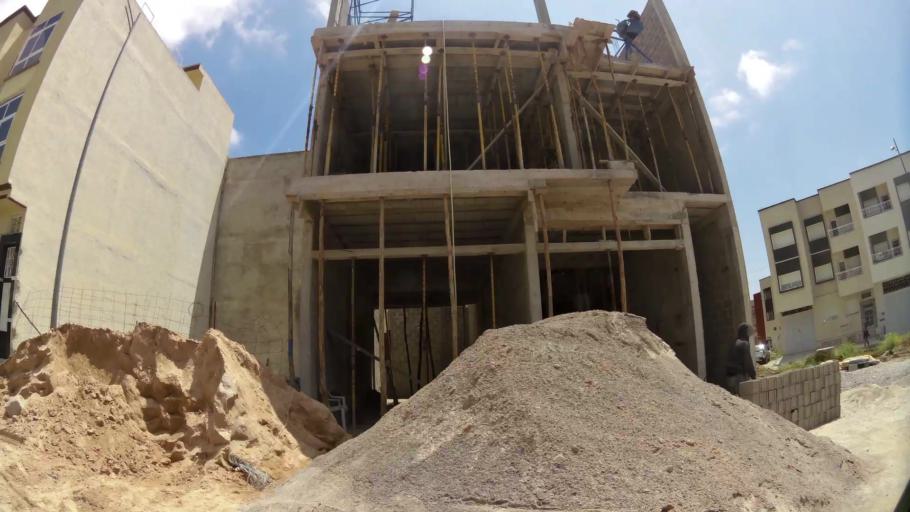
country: MA
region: Fes-Boulemane
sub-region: Fes
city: Fes
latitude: 34.0564
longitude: -5.0422
